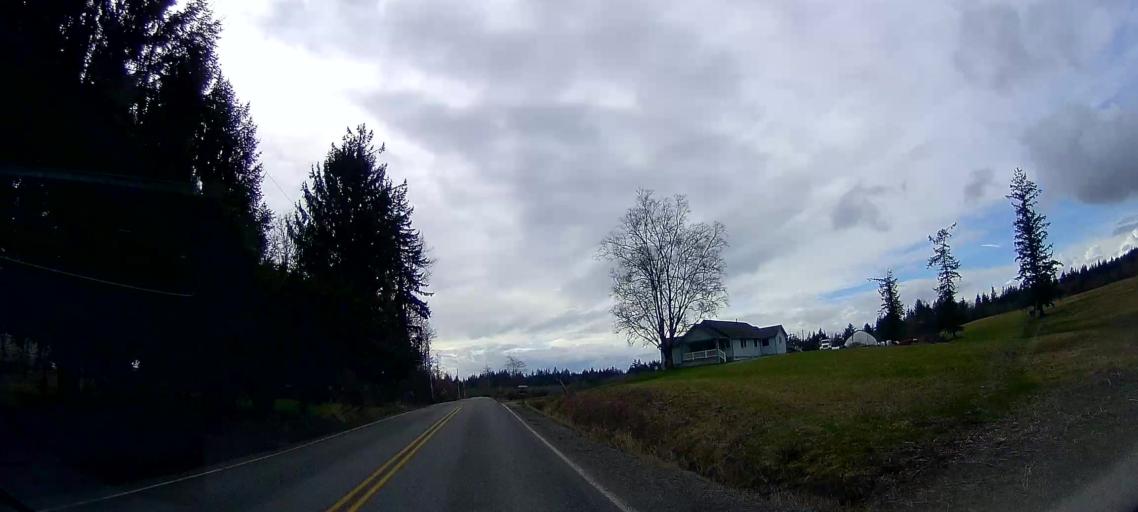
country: US
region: Washington
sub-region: Skagit County
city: Burlington
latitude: 48.5903
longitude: -122.3578
